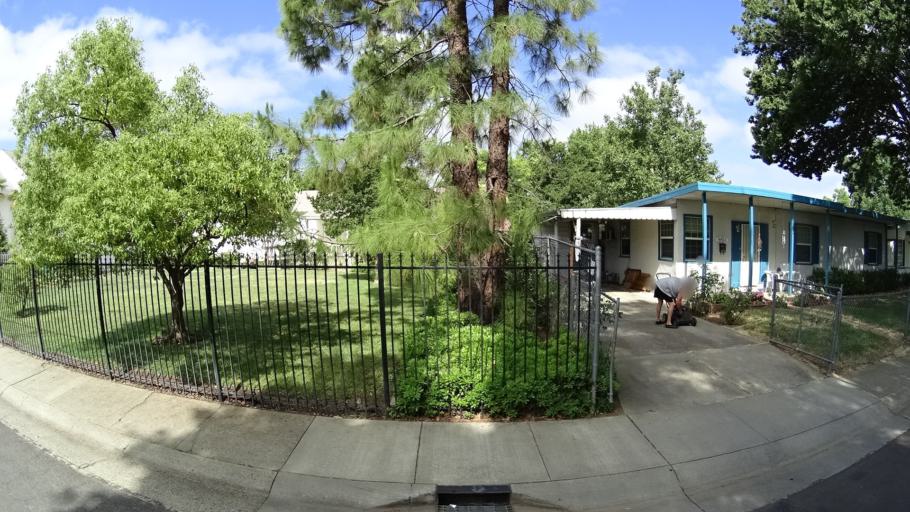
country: US
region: California
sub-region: Sacramento County
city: Parkway
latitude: 38.5347
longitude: -121.4855
